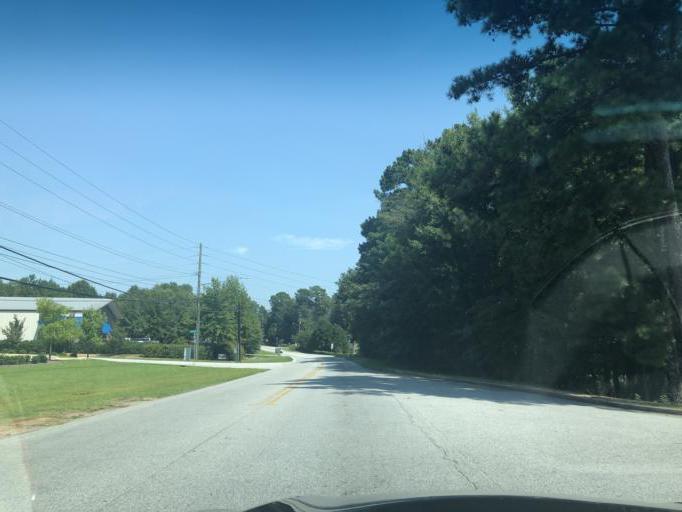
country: US
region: Georgia
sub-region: Muscogee County
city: Columbus
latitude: 32.5139
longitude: -84.9163
